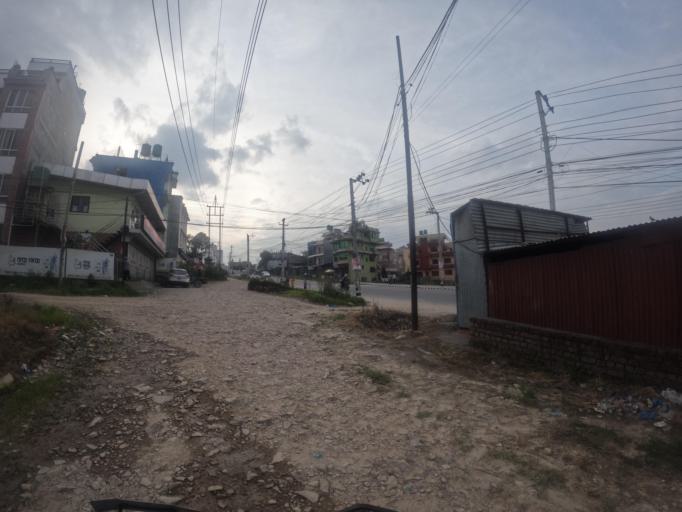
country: NP
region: Central Region
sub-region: Bagmati Zone
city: Bhaktapur
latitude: 27.6808
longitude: 85.3940
